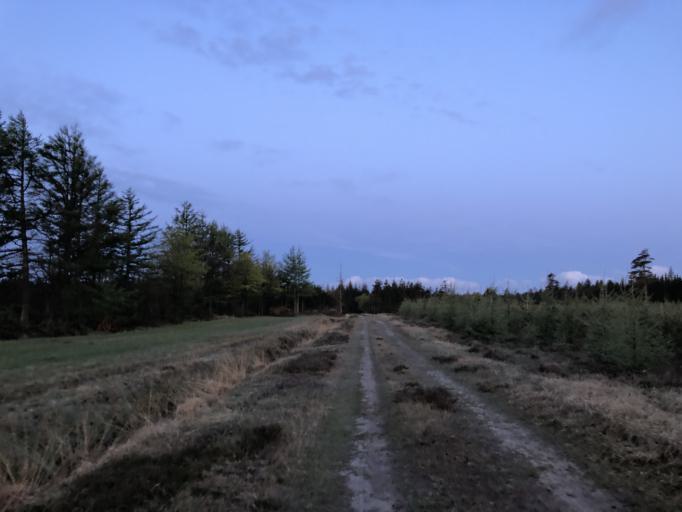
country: DK
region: Central Jutland
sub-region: Holstebro Kommune
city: Ulfborg
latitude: 56.2651
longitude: 8.3986
